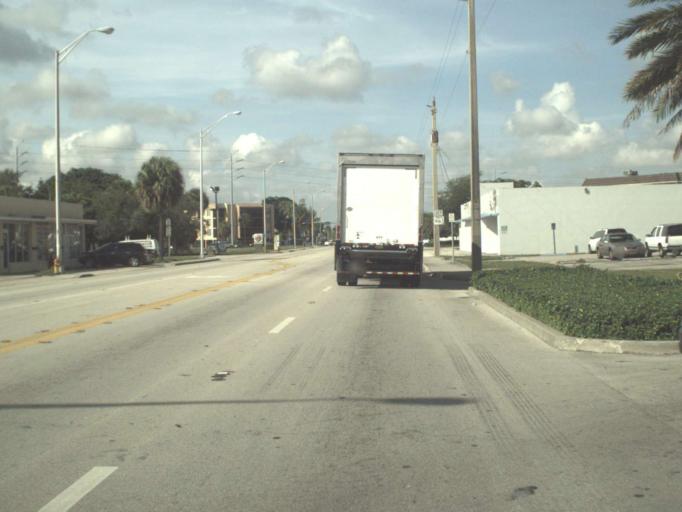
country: US
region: Florida
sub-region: Miami-Dade County
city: North Miami
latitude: 25.9016
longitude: -80.1770
